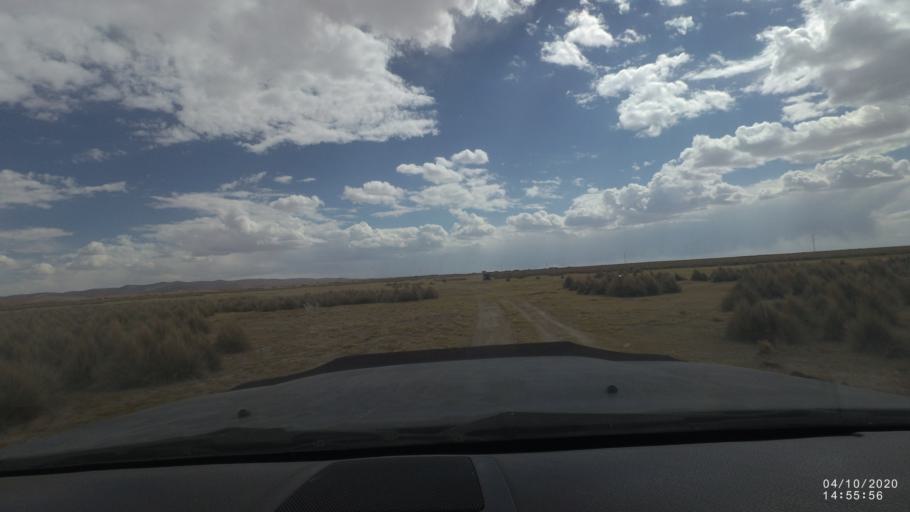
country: BO
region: Oruro
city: Poopo
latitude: -18.6839
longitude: -67.5144
